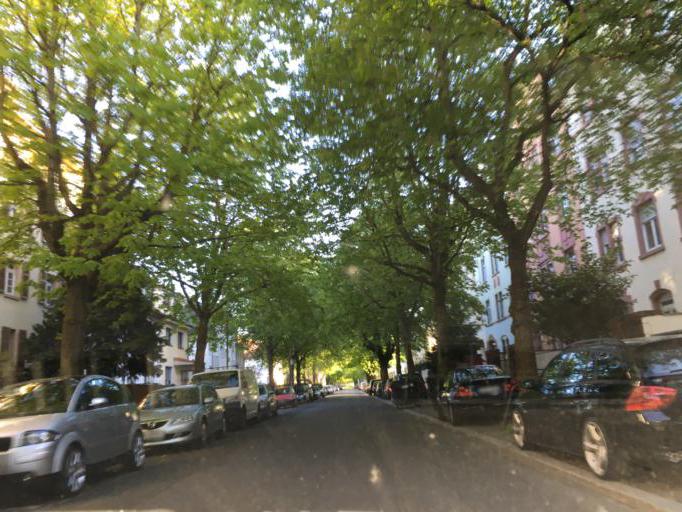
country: DE
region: Hesse
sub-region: Regierungsbezirk Darmstadt
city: Offenbach
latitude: 50.1006
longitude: 8.7724
